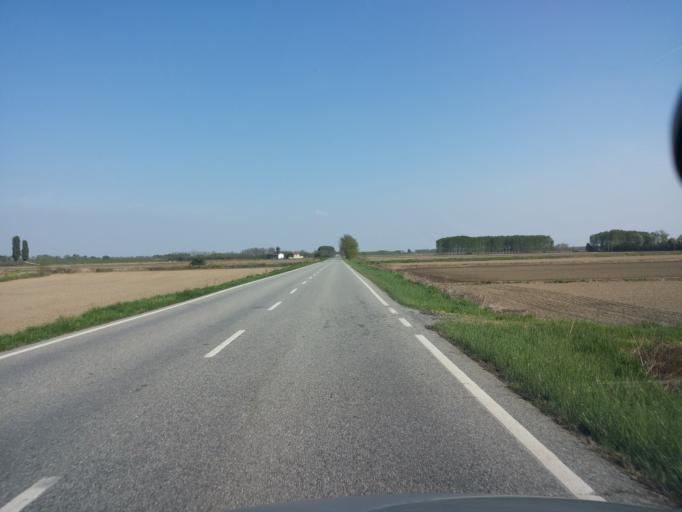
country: IT
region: Piedmont
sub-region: Provincia di Vercelli
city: Motta De Conti
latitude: 45.2108
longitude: 8.5213
